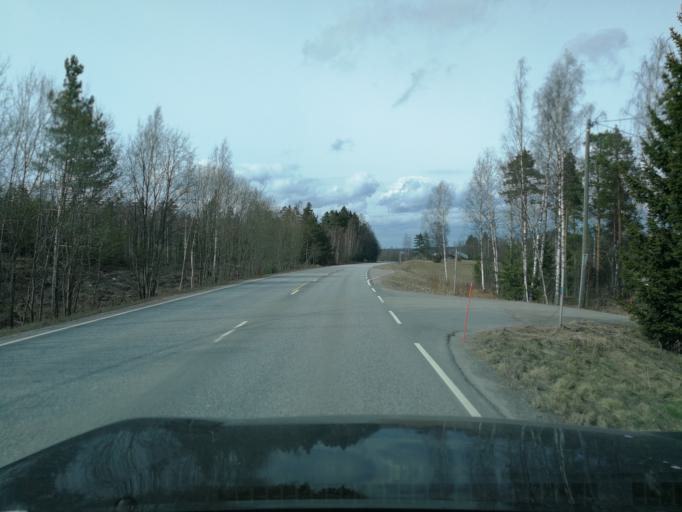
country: FI
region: Uusimaa
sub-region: Helsinki
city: Siuntio
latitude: 60.1028
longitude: 24.2486
